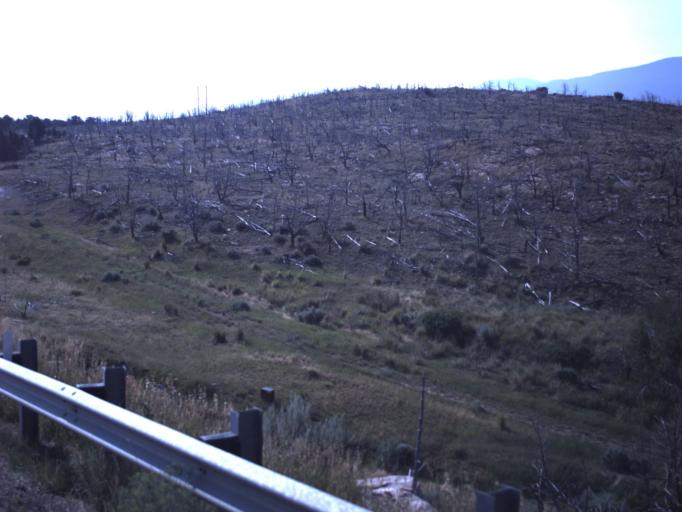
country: US
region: Utah
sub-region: Daggett County
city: Manila
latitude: 40.9419
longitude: -109.4155
